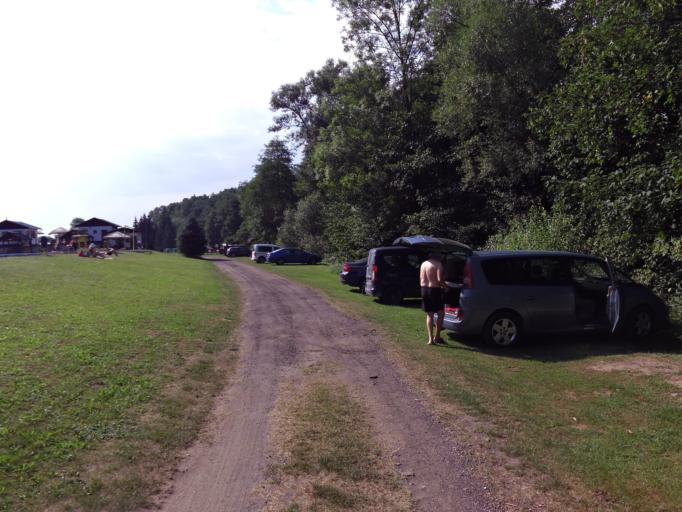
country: CZ
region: Central Bohemia
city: Mnichovo Hradiste
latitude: 50.5315
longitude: 14.9408
